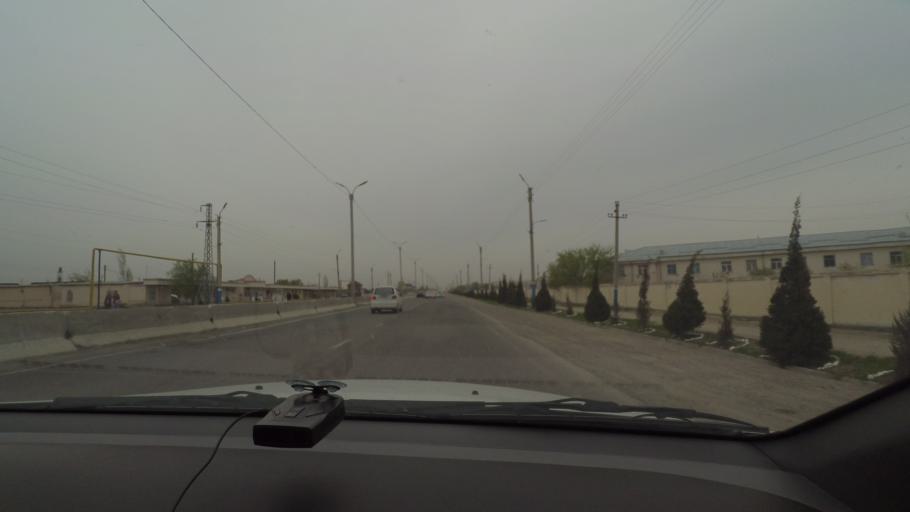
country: KZ
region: Ongtustik Qazaqstan
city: Myrzakent
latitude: 40.5454
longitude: 68.4114
